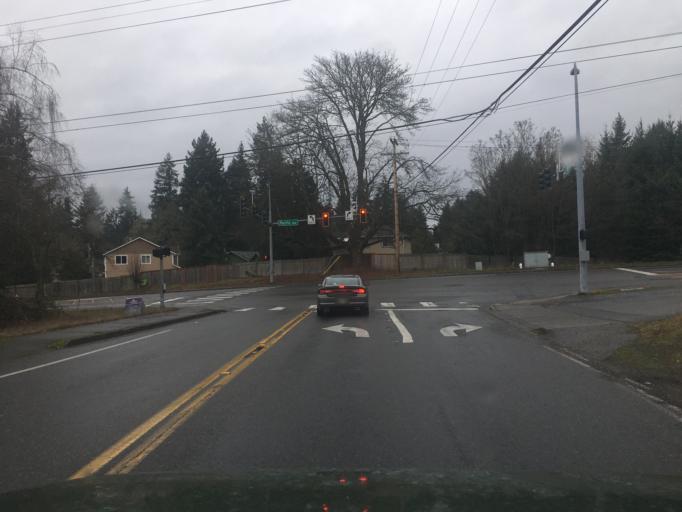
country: US
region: Washington
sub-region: Thurston County
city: Tanglewilde-Thompson Place
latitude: 47.0420
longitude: -122.7823
